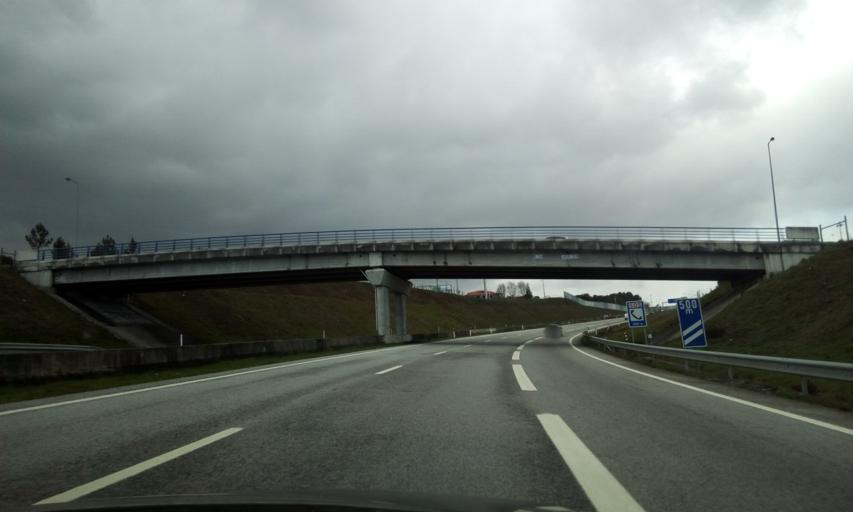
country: PT
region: Viseu
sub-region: Viseu
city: Rio de Loba
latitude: 40.6322
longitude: -7.8430
